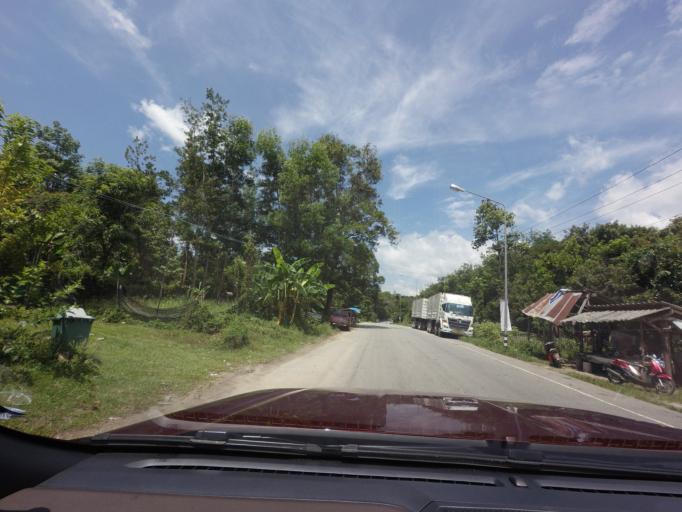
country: TH
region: Narathiwat
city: Ra-ngae
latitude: 6.2476
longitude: 101.6842
